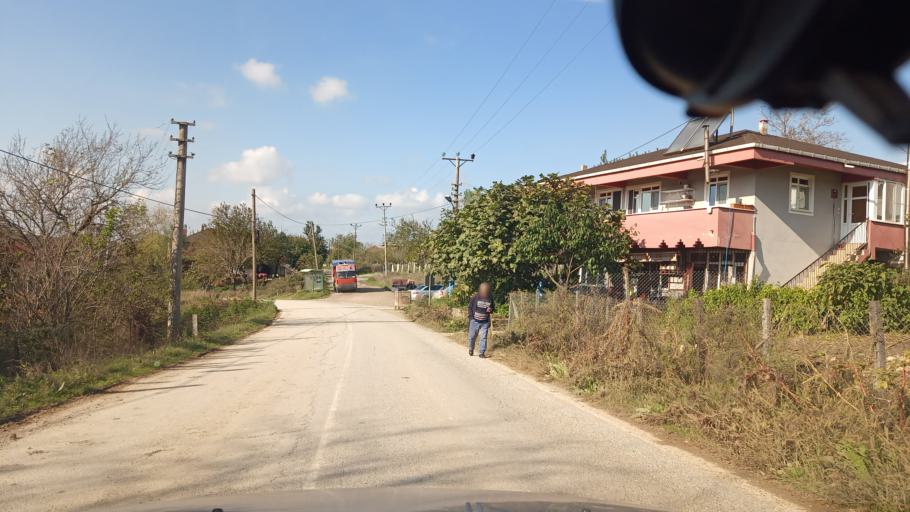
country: TR
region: Sakarya
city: Ferizli
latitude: 41.1071
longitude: 30.4821
